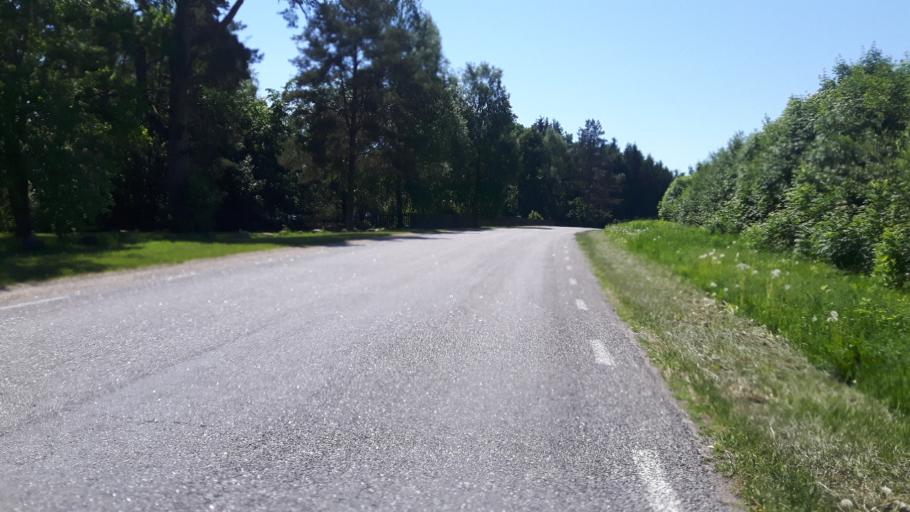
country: EE
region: Paernumaa
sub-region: Tootsi vald
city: Tootsi
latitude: 58.4861
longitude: 24.8283
